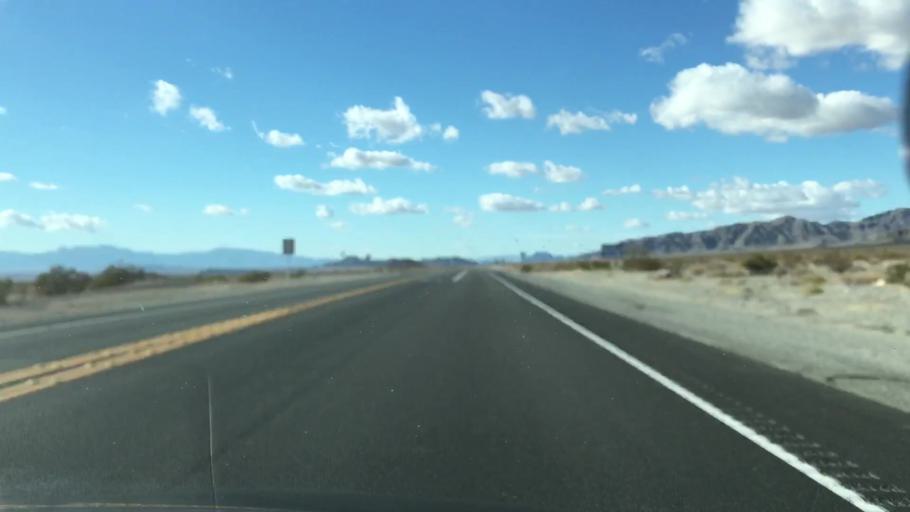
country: US
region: Nevada
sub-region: Nye County
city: Pahrump
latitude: 36.5646
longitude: -116.1215
